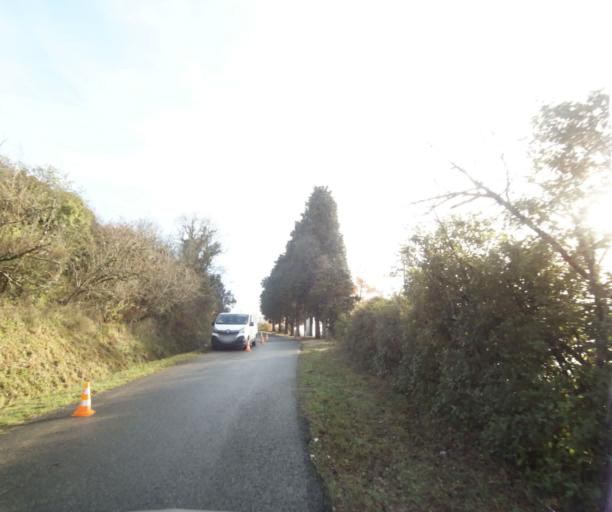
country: FR
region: Midi-Pyrenees
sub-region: Departement de la Haute-Garonne
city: Villemur-sur-Tarn
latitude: 43.8615
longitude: 1.5103
